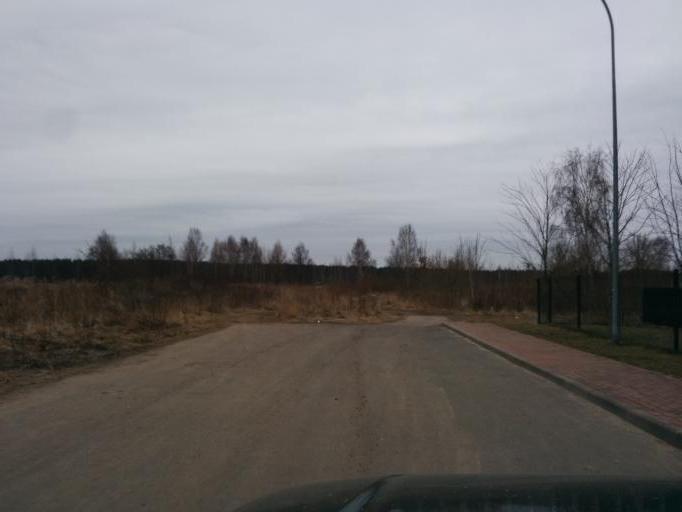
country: LV
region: Jurmala
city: Jurmala
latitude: 56.9611
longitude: 23.8195
